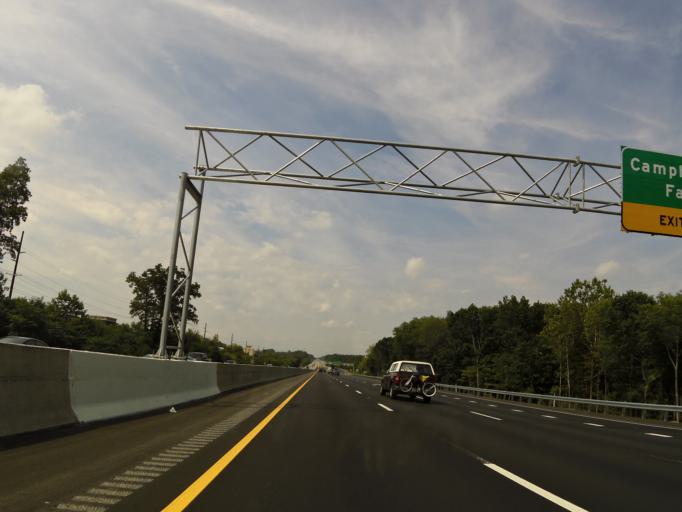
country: US
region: Tennessee
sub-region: Knox County
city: Farragut
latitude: 35.9012
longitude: -84.1653
